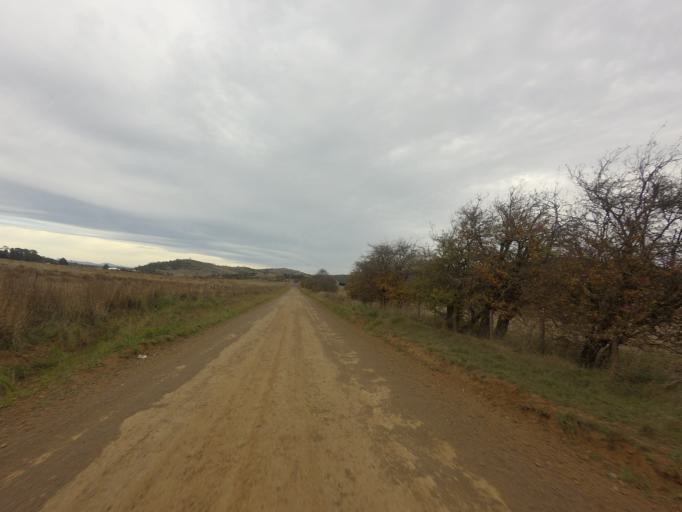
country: AU
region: Tasmania
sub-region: Derwent Valley
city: New Norfolk
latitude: -42.5357
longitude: 146.9421
